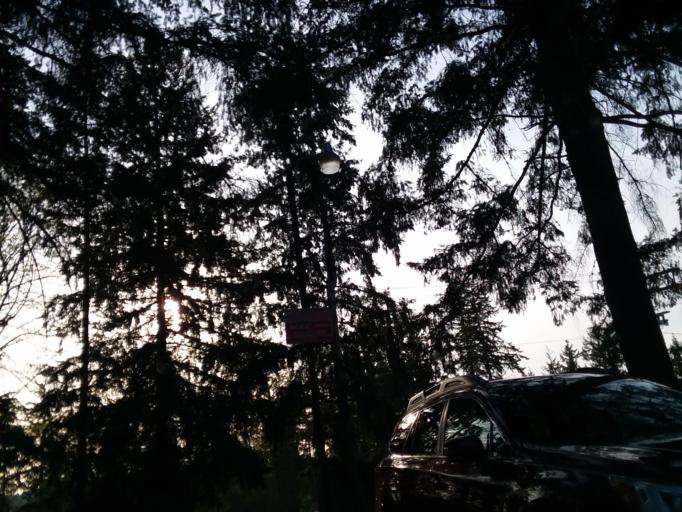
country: US
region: Washington
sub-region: King County
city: Redmond
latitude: 47.7029
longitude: -122.1317
